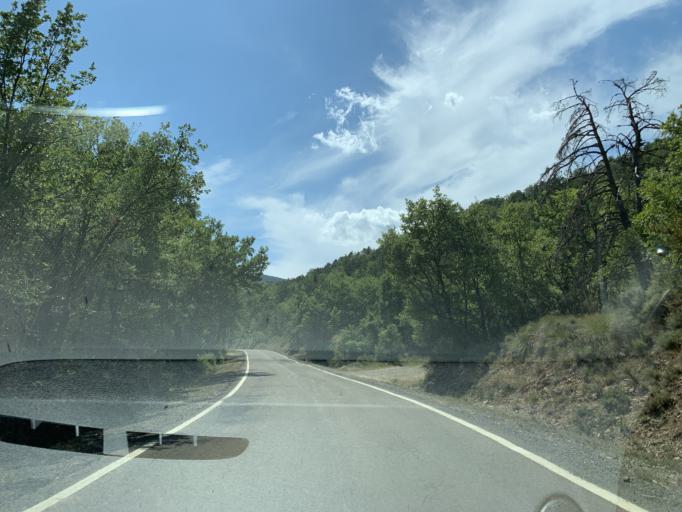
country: ES
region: Aragon
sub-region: Provincia de Huesca
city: Jasa
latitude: 42.6221
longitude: -0.6587
